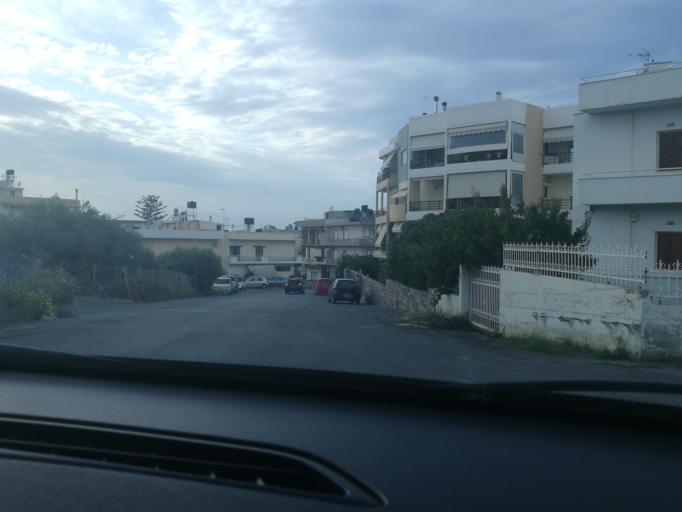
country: GR
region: Crete
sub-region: Nomos Irakleiou
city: Irakleion
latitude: 35.3145
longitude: 25.1399
